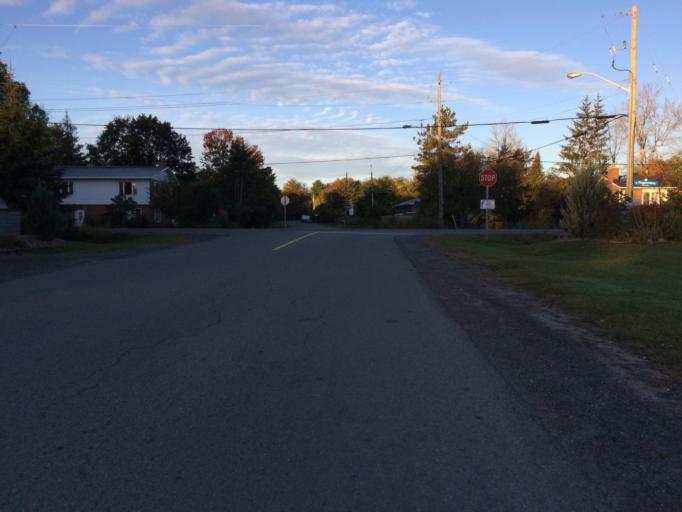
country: CA
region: Ontario
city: Ottawa
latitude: 45.2598
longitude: -75.5953
